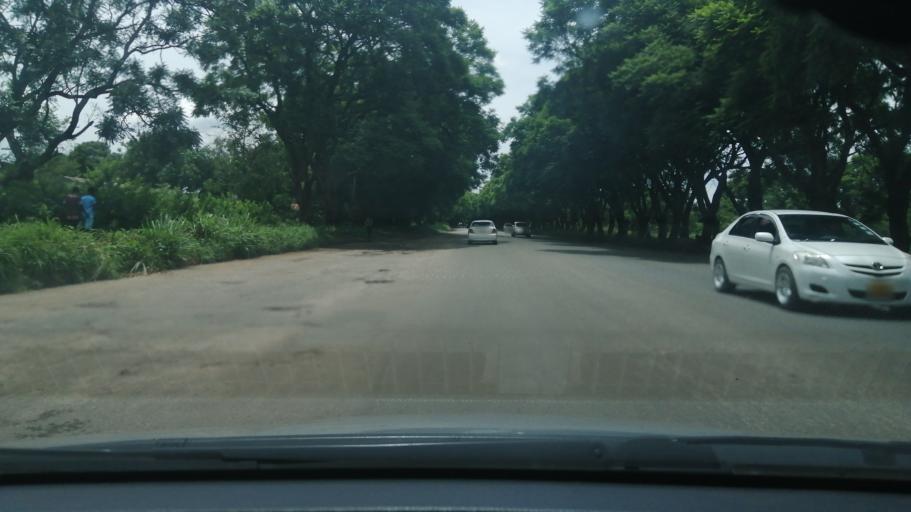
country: ZW
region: Harare
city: Harare
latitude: -17.8076
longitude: 31.0402
